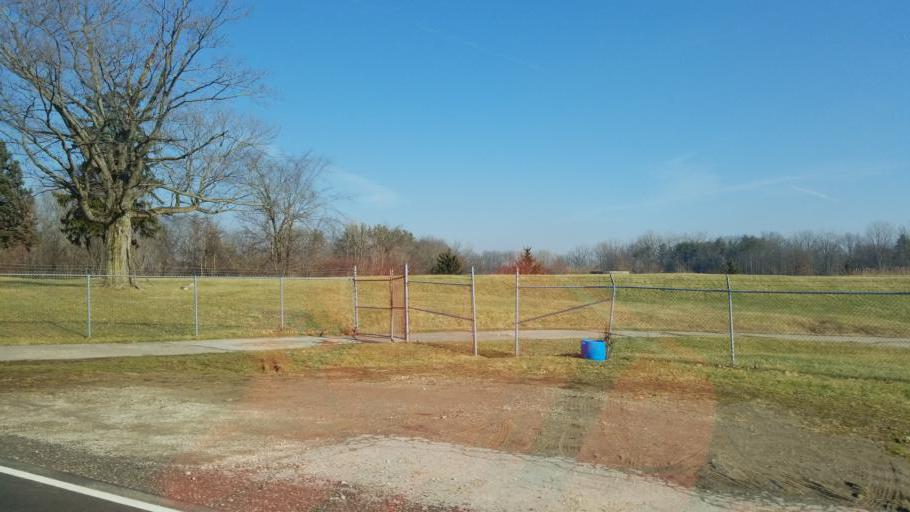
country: US
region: Ohio
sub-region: Crawford County
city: Bucyrus
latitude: 40.8275
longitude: -82.9402
